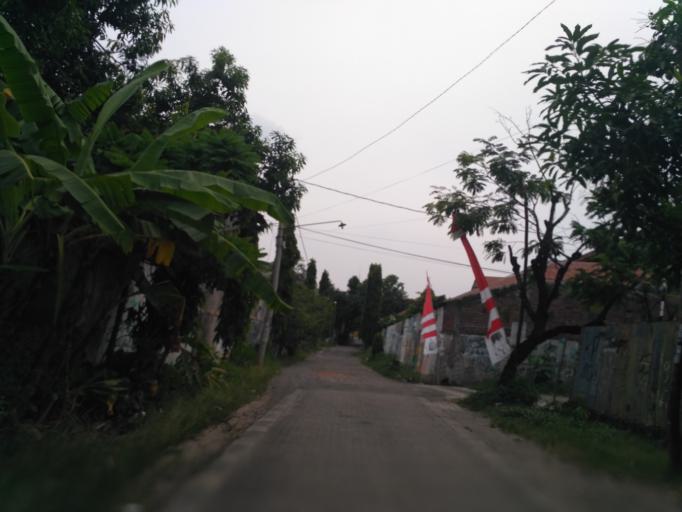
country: ID
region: Central Java
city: Semarang
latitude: -7.0646
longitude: 110.4181
